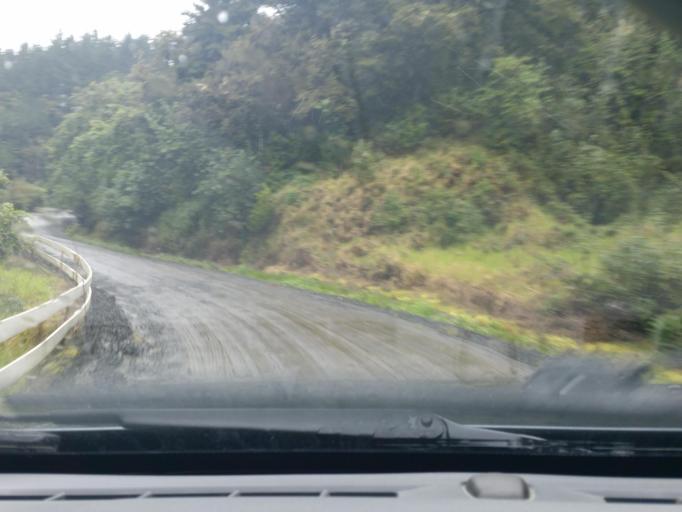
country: NZ
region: Northland
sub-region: Kaipara District
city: Dargaville
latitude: -35.8291
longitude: 173.8270
